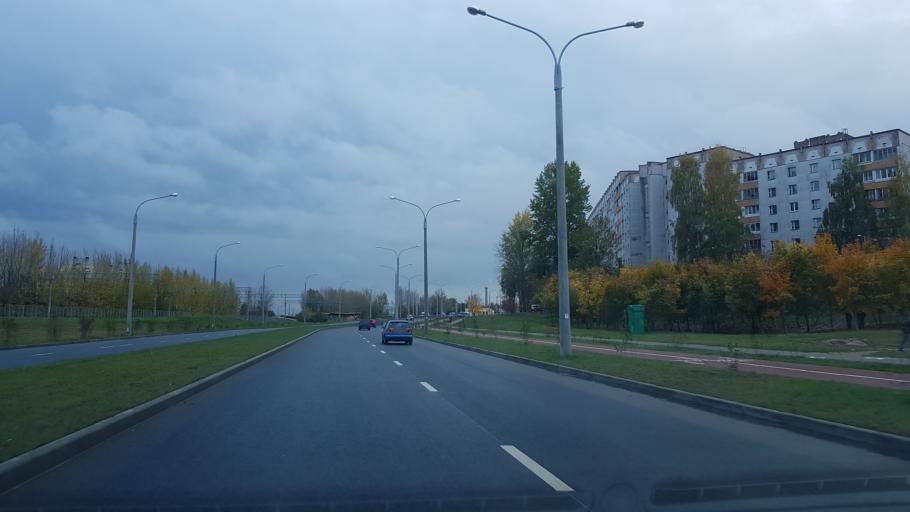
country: BY
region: Minsk
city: Syenitsa
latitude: 53.8544
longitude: 27.5561
